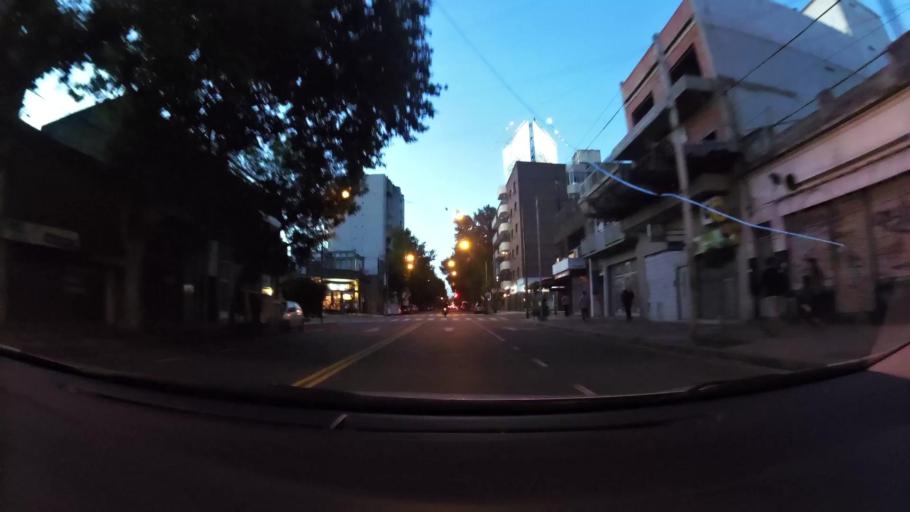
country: AR
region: Buenos Aires F.D.
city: Villa Santa Rita
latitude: -34.6398
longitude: -58.4582
